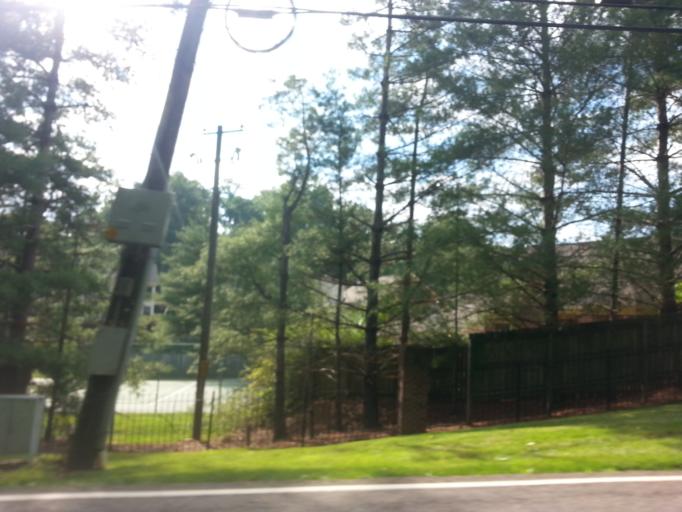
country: US
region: Tennessee
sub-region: Blount County
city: Louisville
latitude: 35.8912
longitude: -84.0351
